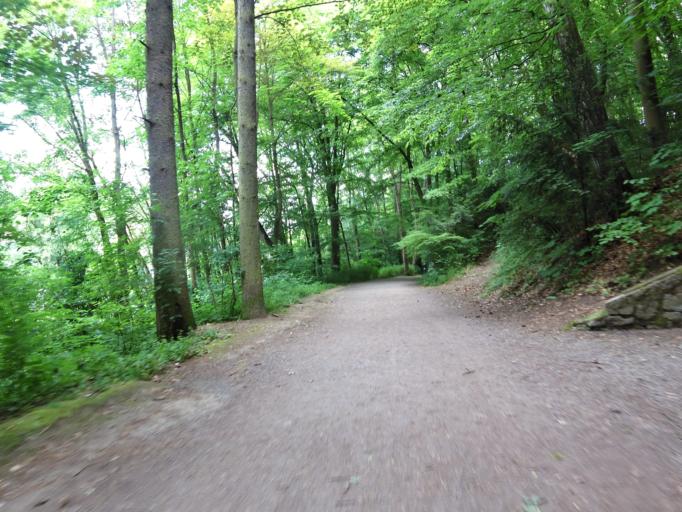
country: DE
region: Bavaria
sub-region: Regierungsbezirk Unterfranken
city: Wuerzburg
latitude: 49.7736
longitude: 9.9248
